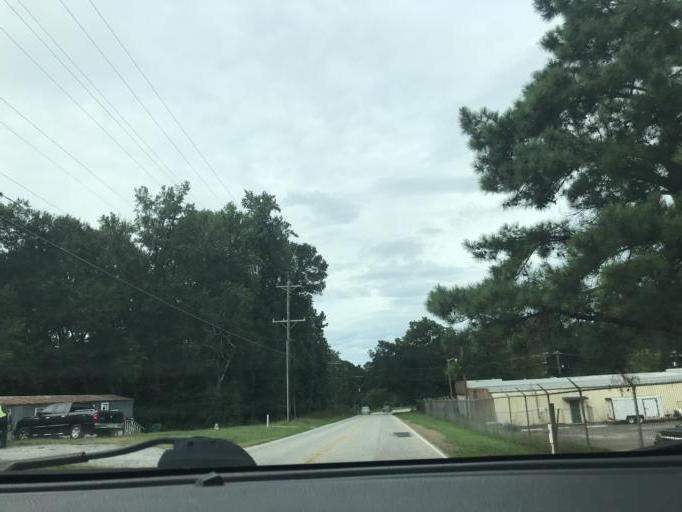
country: US
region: South Carolina
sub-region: Cherokee County
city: East Gaffney
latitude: 35.1055
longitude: -81.6538
